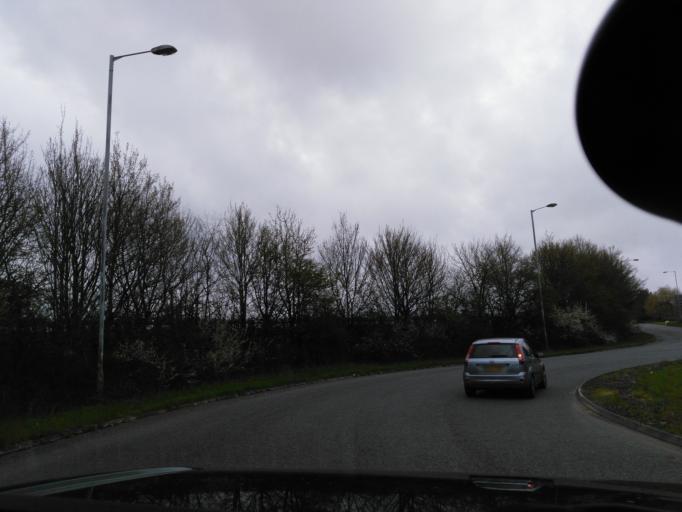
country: GB
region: England
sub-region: Somerset
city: Frome
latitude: 51.2083
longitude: -2.3161
